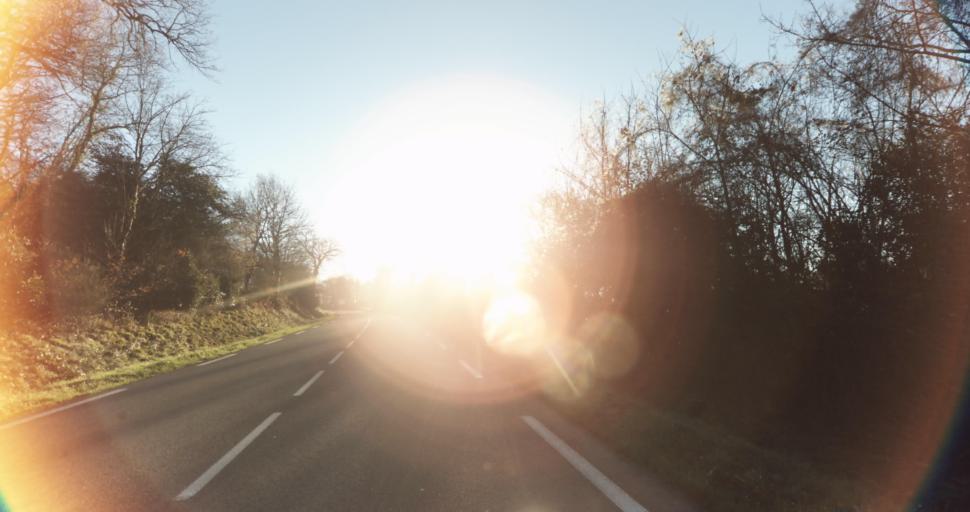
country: FR
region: Aquitaine
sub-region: Departement des Pyrenees-Atlantiques
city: Morlaas
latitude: 43.3317
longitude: -0.2798
